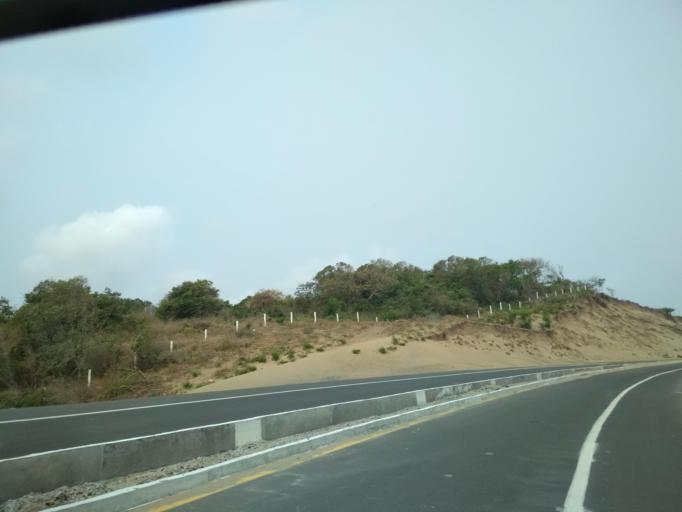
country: MX
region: Veracruz
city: Anton Lizardo
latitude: 19.0428
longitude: -95.9930
